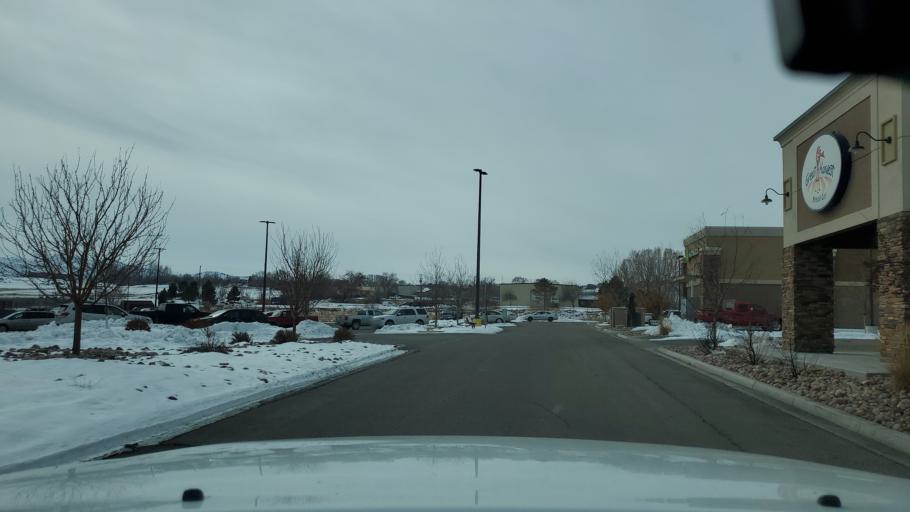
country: US
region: Utah
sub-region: Uintah County
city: Vernal
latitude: 40.4358
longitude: -109.5683
